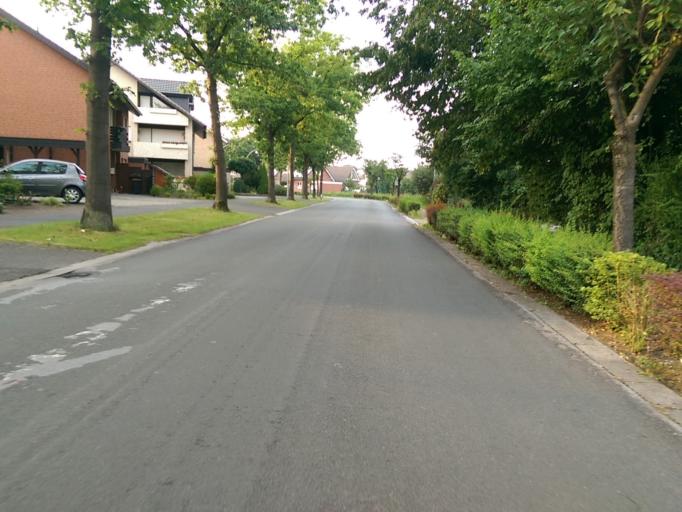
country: DE
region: North Rhine-Westphalia
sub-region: Regierungsbezirk Detmold
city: Rheda-Wiedenbruck
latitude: 51.8859
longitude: 8.2346
